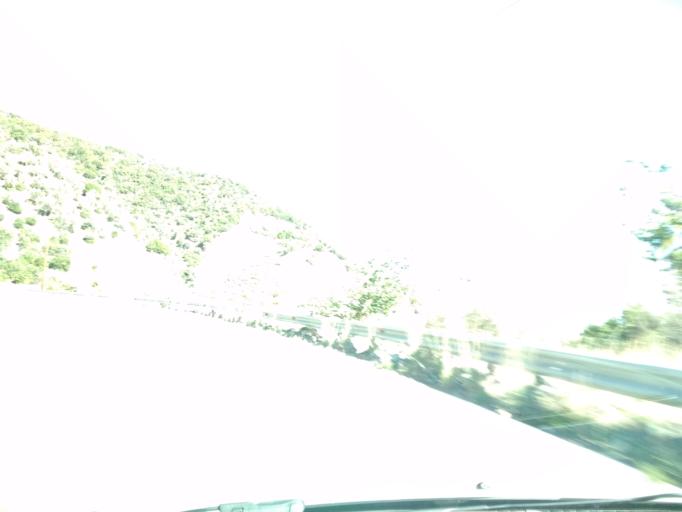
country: GR
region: Central Greece
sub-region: Nomos Evvoias
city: Oreoi
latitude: 38.8427
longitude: 23.0767
